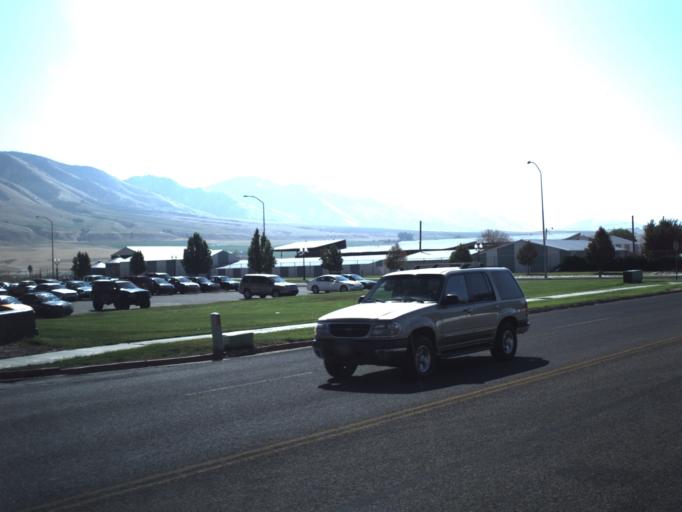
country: US
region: Utah
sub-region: Cache County
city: Hyrum
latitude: 41.6281
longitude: -111.8327
